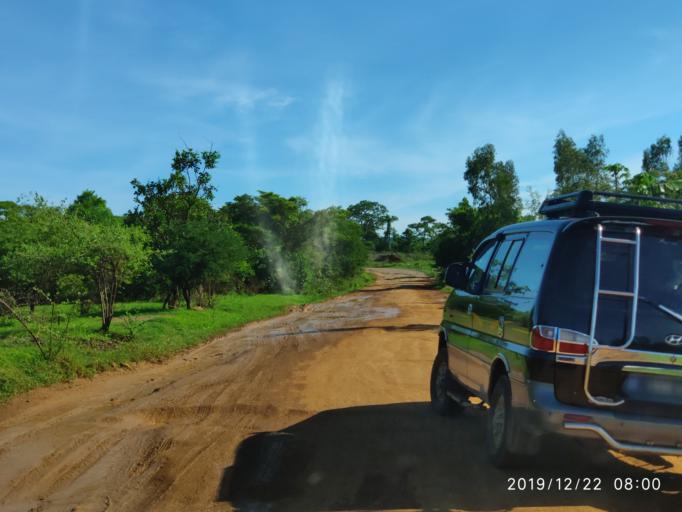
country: MG
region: Diana
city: Ambilobe
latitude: -12.9482
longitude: 49.1499
